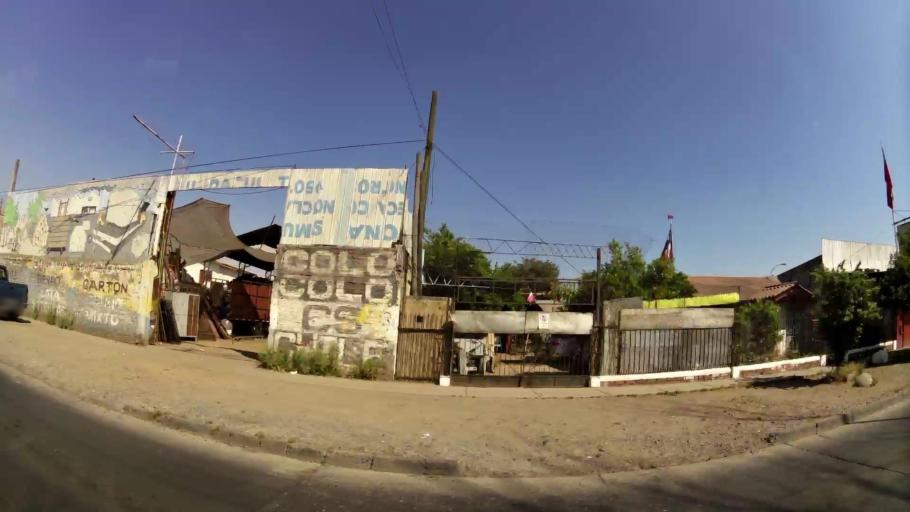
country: CL
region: Santiago Metropolitan
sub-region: Provincia de Santiago
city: La Pintana
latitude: -33.5467
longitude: -70.6119
